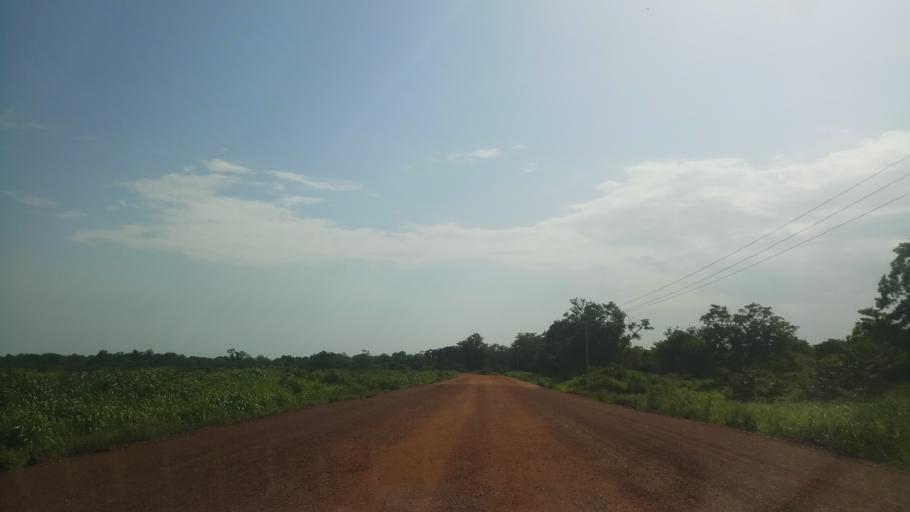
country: ET
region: Gambela
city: Gambela
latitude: 8.1620
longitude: 34.3128
